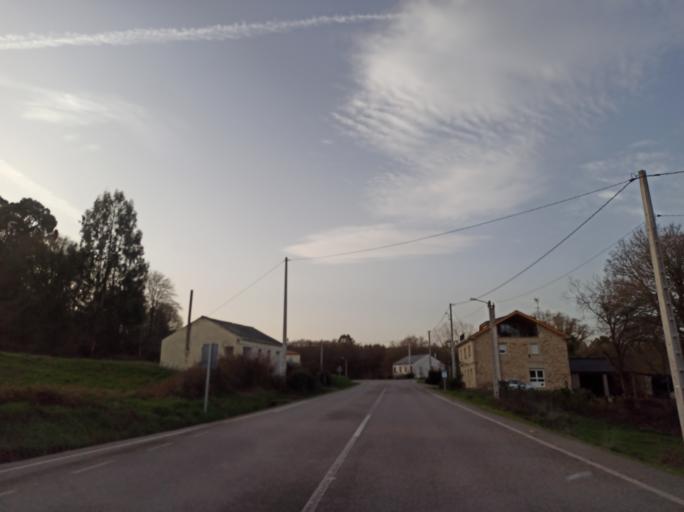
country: ES
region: Galicia
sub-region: Provincia de Lugo
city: Friol
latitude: 43.0248
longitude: -7.8664
